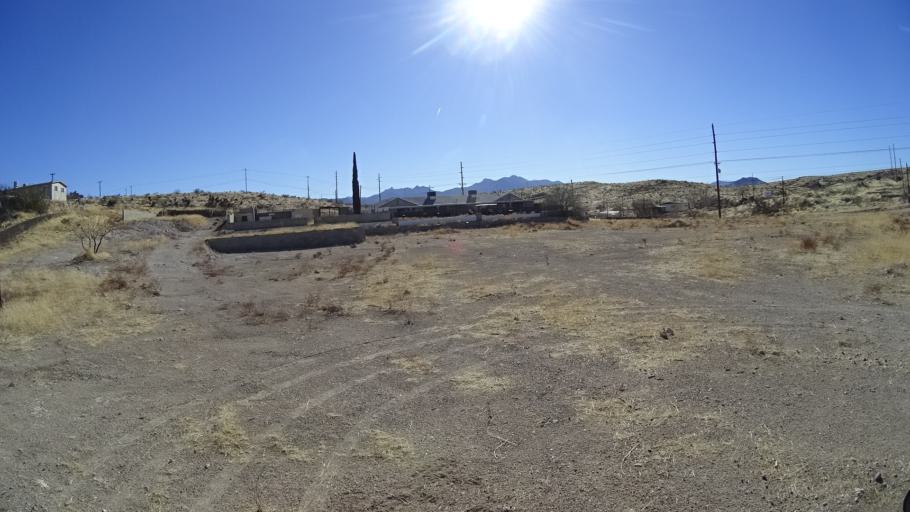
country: US
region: Arizona
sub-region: Mohave County
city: Kingman
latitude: 35.1860
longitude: -114.0578
